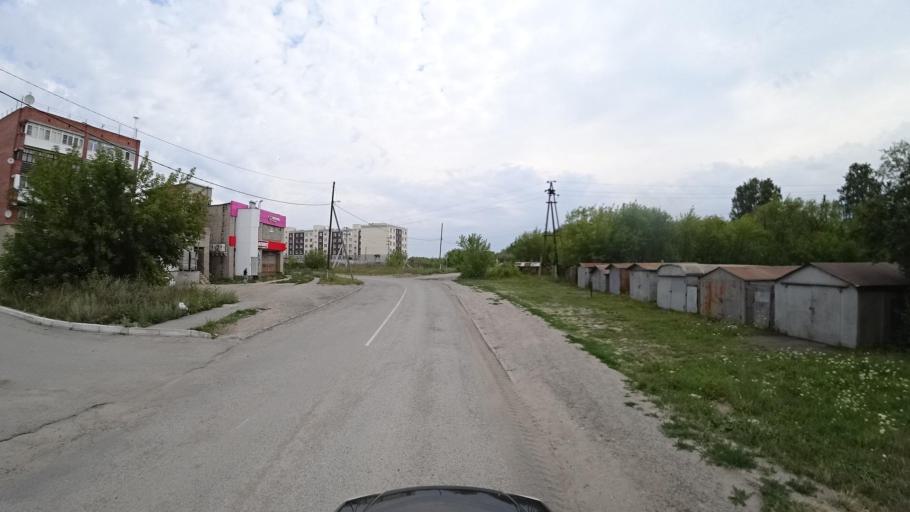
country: RU
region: Sverdlovsk
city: Kamyshlov
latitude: 56.8449
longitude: 62.7448
